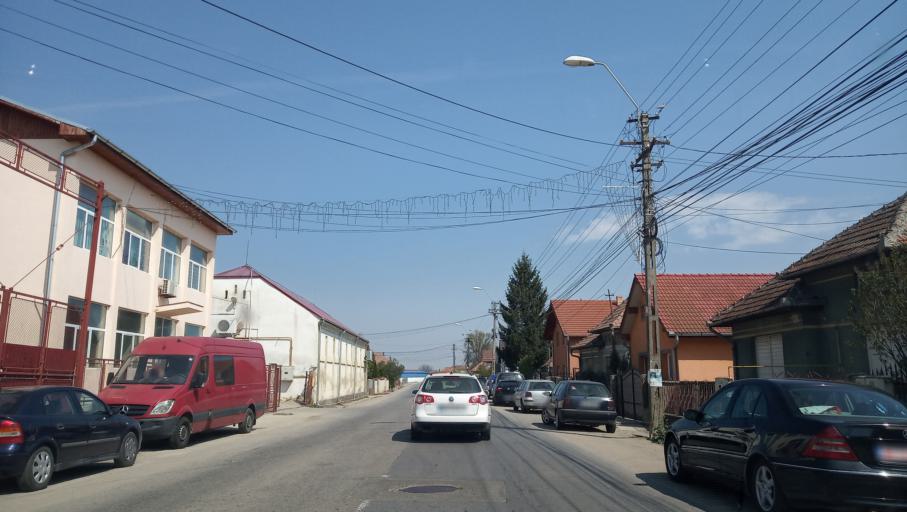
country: RO
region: Alba
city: Vurpar
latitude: 45.9950
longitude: 23.4866
